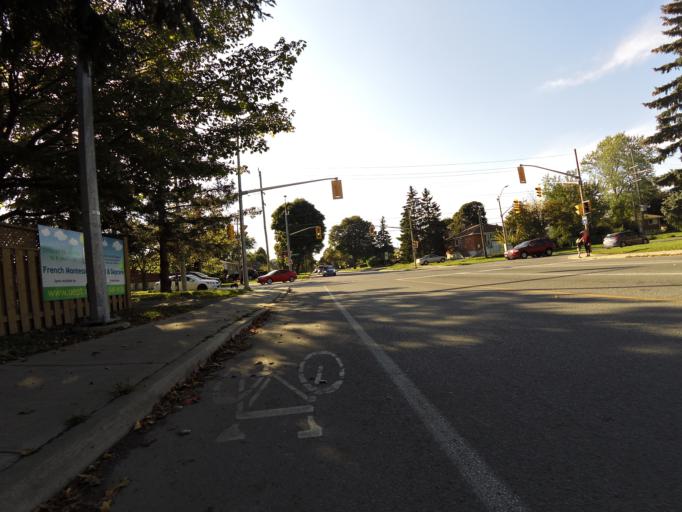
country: CA
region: Ontario
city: Kingston
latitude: 44.2301
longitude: -76.5258
